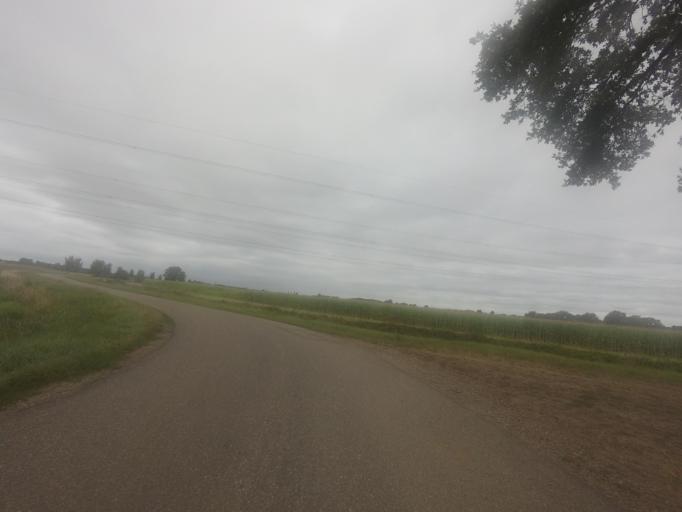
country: NL
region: North Brabant
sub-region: Gemeente Grave
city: Grave
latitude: 51.7864
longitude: 5.7485
